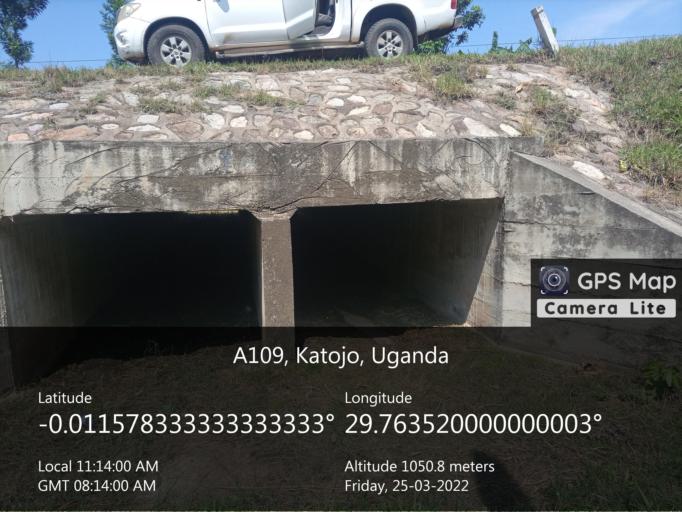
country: UG
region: Western Region
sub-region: Kasese District
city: Kilembe
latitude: -0.0116
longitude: 29.7635
